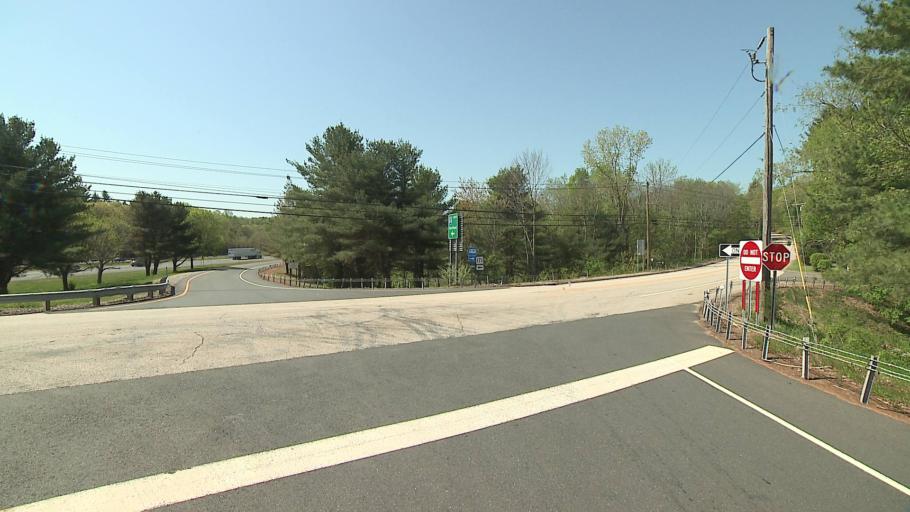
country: US
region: Massachusetts
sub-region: Hampden County
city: Holland
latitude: 41.9761
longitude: -72.1839
